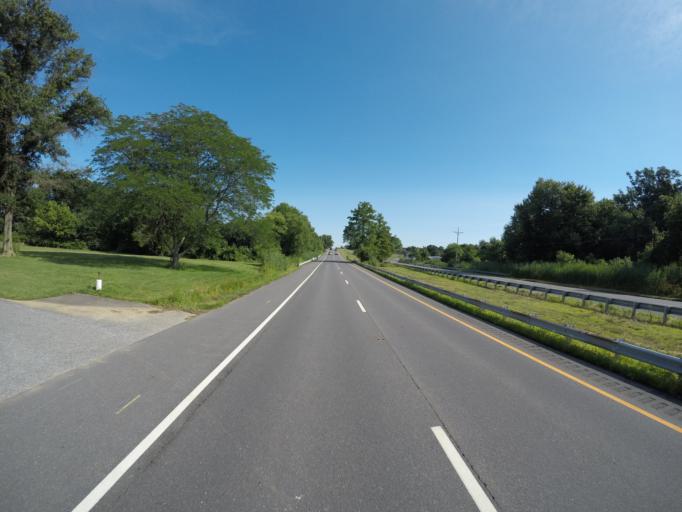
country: US
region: Delaware
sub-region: New Castle County
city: Bear
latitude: 39.5685
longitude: -75.6549
